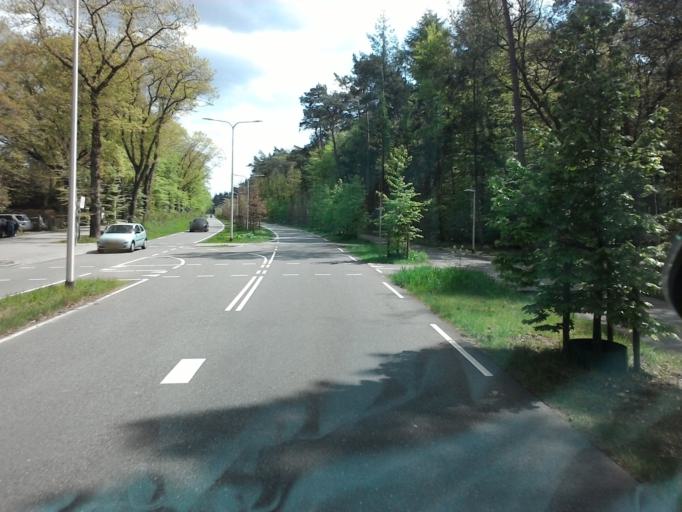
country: NL
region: Utrecht
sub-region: Gemeente Zeist
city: Zeist
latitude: 52.0967
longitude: 5.2736
